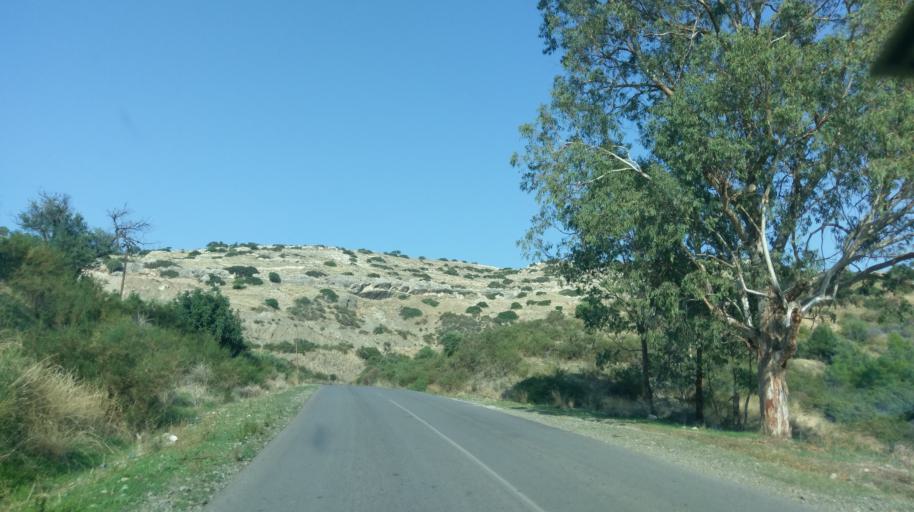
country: CY
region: Lefkosia
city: Kato Pyrgos
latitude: 35.1632
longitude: 32.7508
